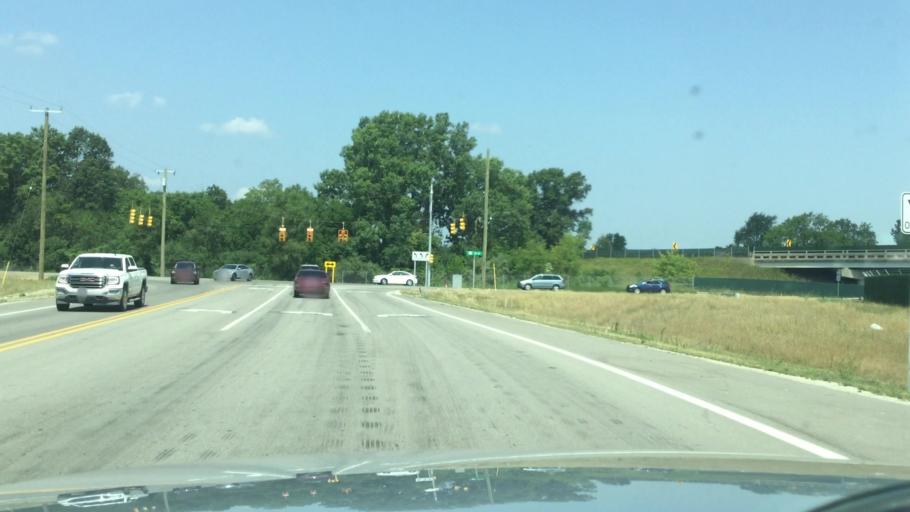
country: US
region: Michigan
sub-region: Washtenaw County
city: Ypsilanti
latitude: 42.2413
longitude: -83.5657
